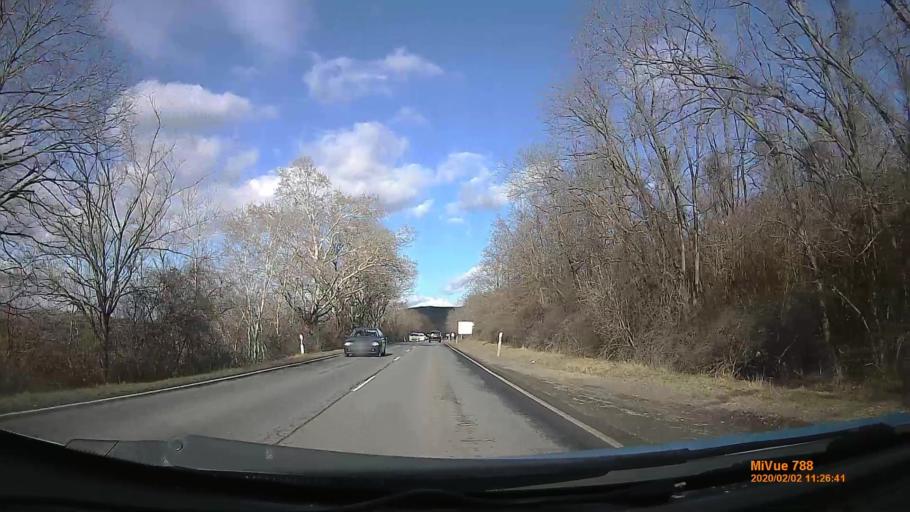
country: HU
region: Gyor-Moson-Sopron
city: Sopron
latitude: 47.7094
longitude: 16.5745
